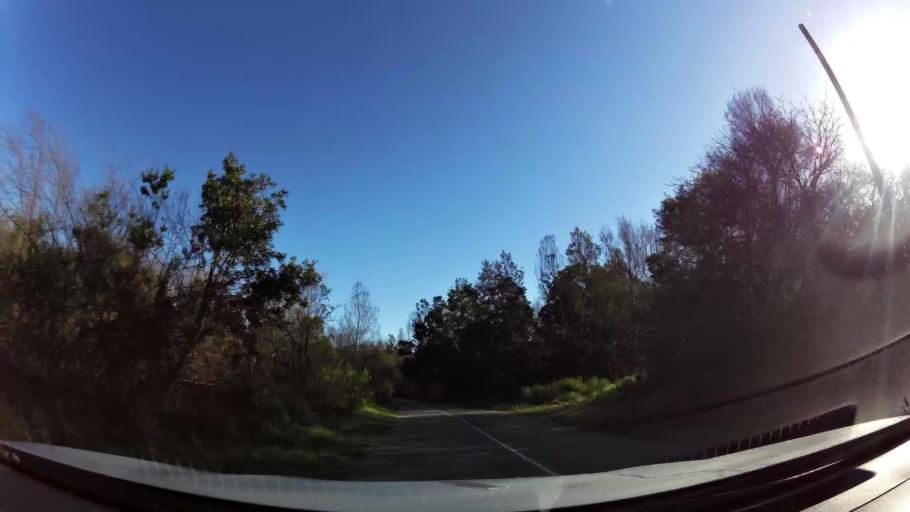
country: ZA
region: Western Cape
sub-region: Eden District Municipality
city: Knysna
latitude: -34.0313
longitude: 23.0146
